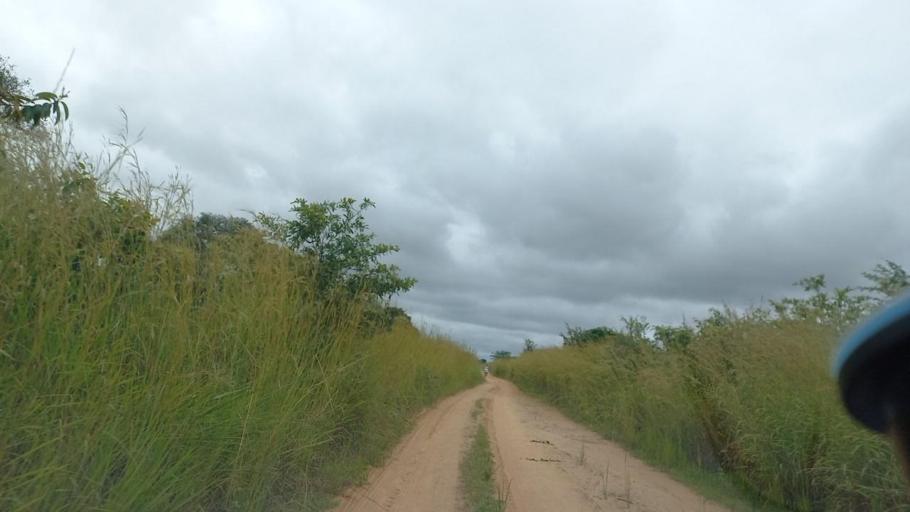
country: ZM
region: Lusaka
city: Lusaka
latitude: -15.1341
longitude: 28.3687
